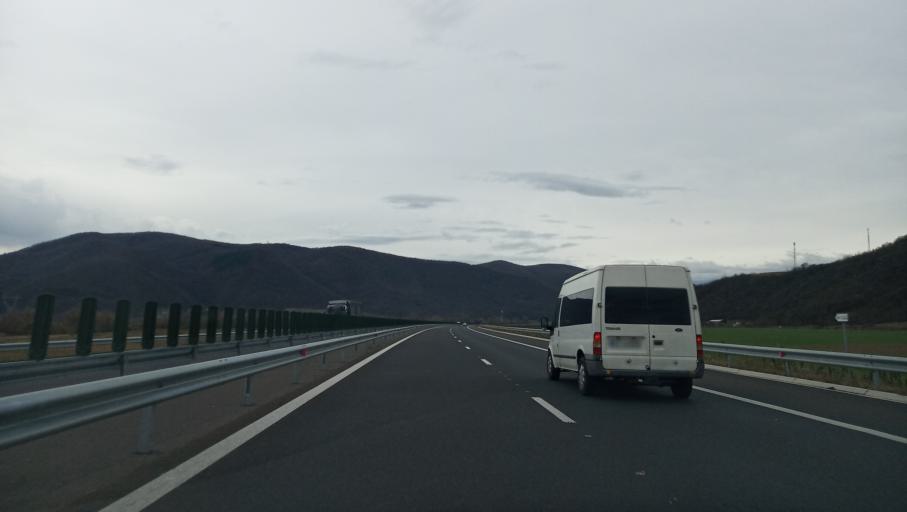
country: RO
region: Hunedoara
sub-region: Comuna Vetel
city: Vetel
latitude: 45.9137
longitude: 22.8065
